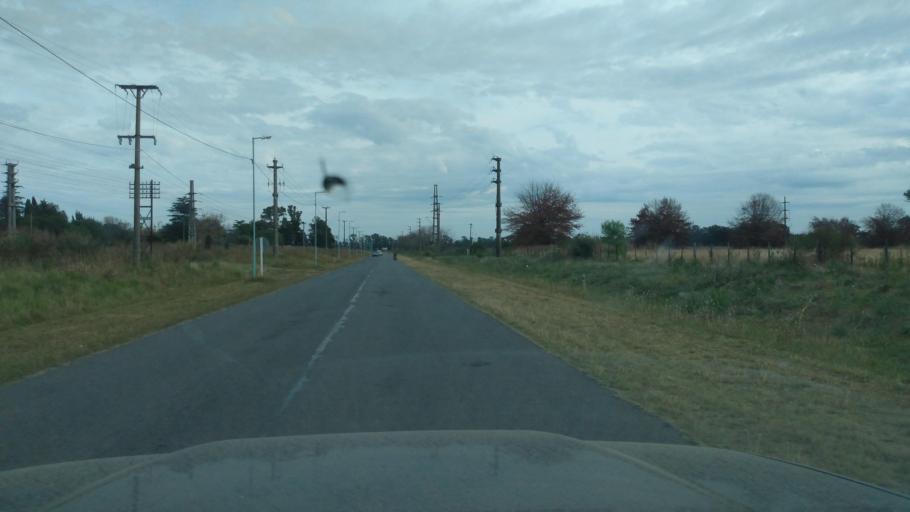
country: AR
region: Buenos Aires
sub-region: Partido de Lujan
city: Lujan
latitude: -34.5882
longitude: -59.1371
